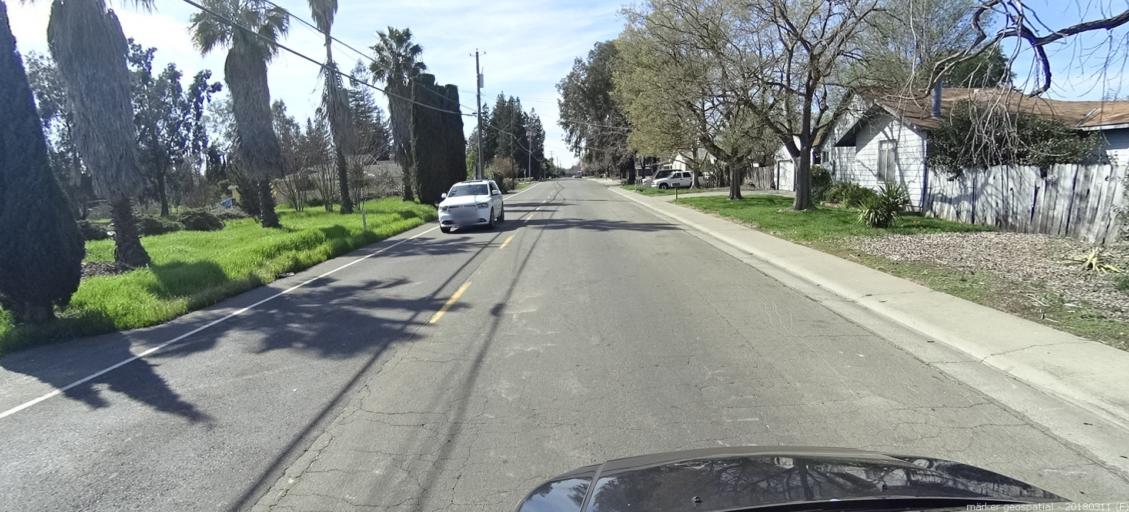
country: US
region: California
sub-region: Sacramento County
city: Florin
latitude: 38.4887
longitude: -121.4318
